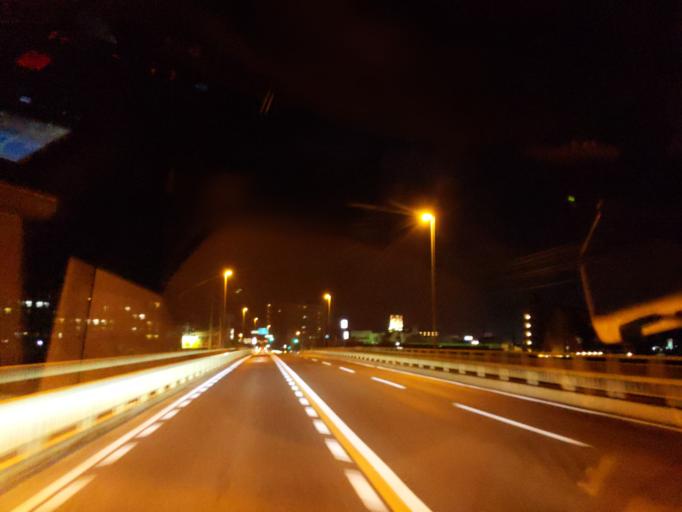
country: JP
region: Okayama
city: Okayama-shi
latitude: 34.6715
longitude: 133.9561
